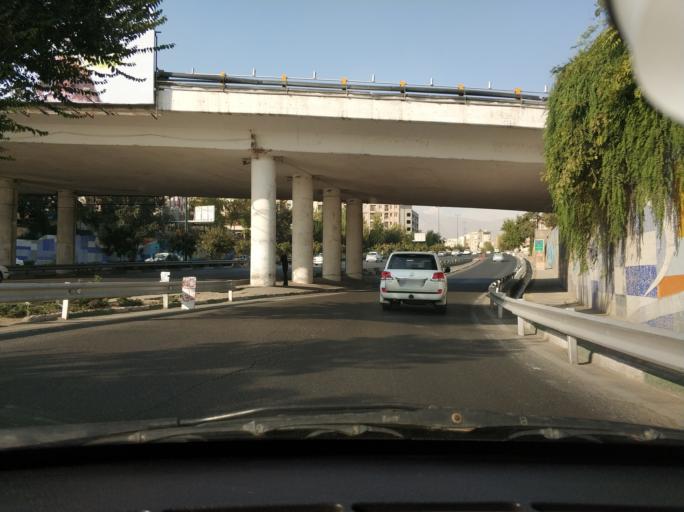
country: IR
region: Tehran
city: Tehran
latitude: 35.7430
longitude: 51.4622
